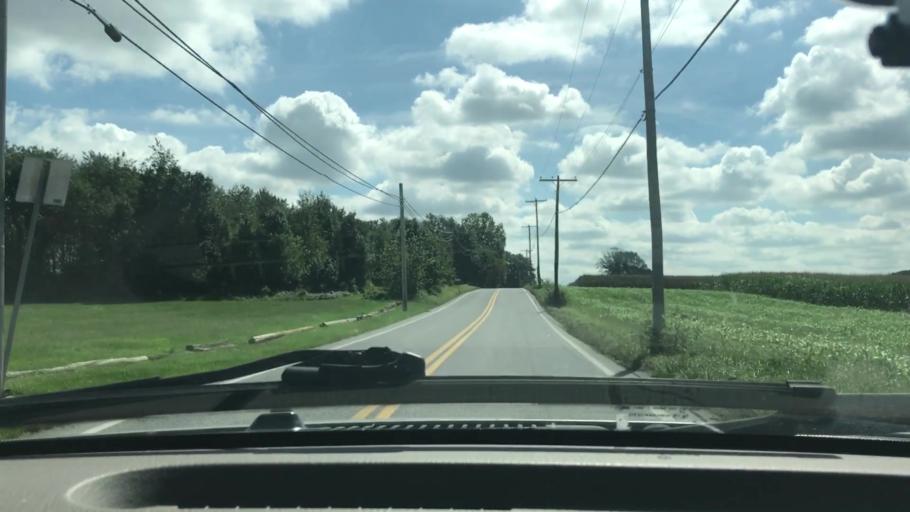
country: US
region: Pennsylvania
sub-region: Lancaster County
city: East Petersburg
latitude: 40.1158
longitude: -76.3791
